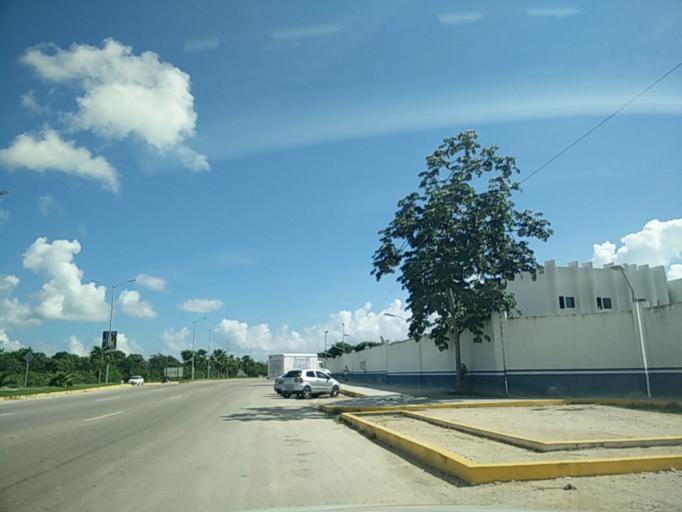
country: MX
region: Quintana Roo
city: Playa del Carmen
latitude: 20.6679
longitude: -87.0658
